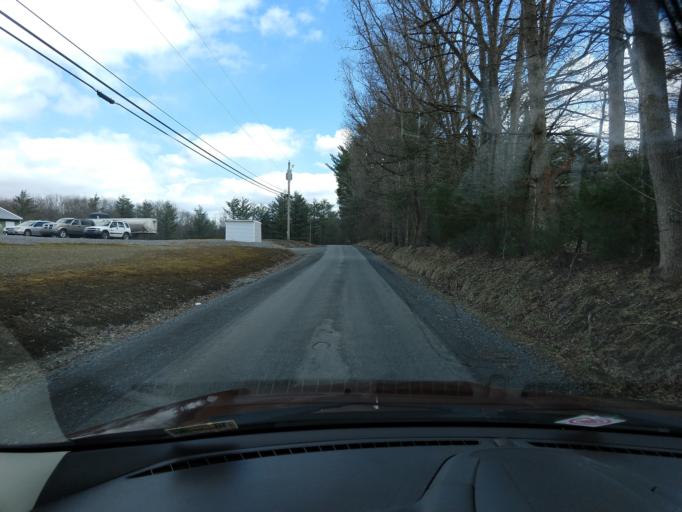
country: US
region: West Virginia
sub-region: Greenbrier County
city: Fairlea
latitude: 37.8277
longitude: -80.5290
